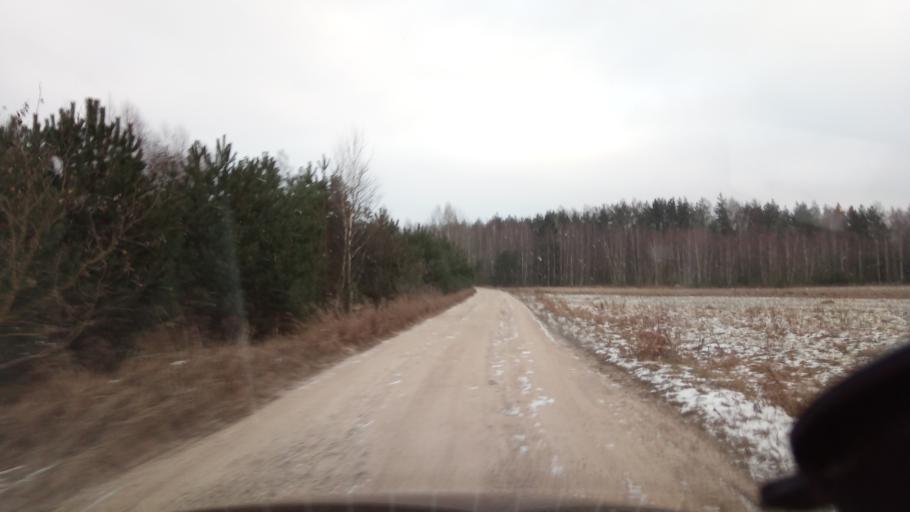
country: LT
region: Alytaus apskritis
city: Varena
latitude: 54.1215
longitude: 24.7042
